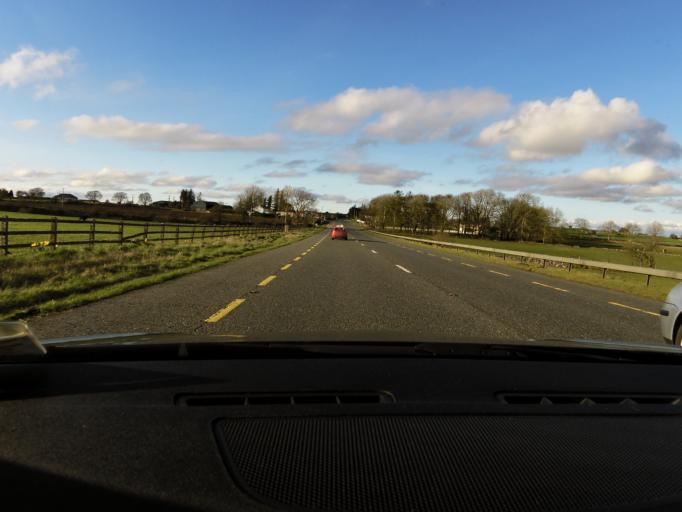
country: IE
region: Connaught
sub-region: Roscommon
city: Roscommon
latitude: 53.6748
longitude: -8.1977
